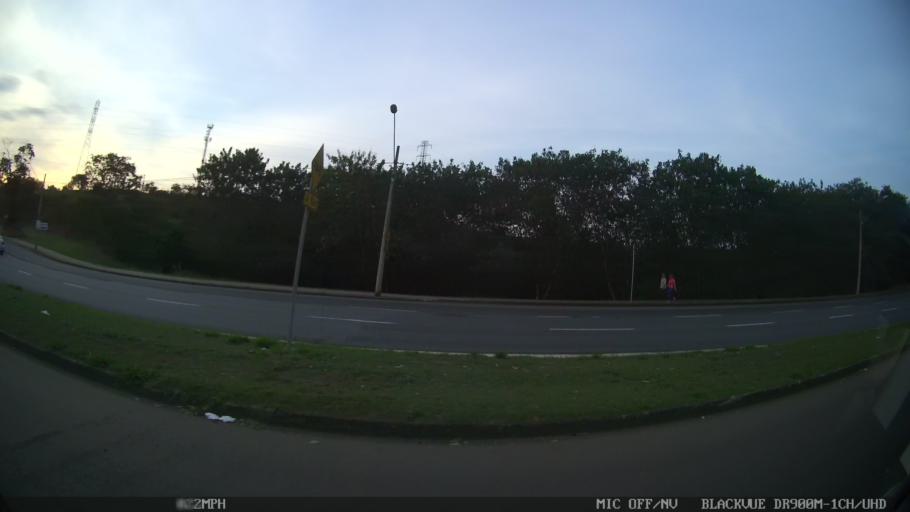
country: BR
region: Sao Paulo
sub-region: Limeira
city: Limeira
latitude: -22.5432
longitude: -47.4041
